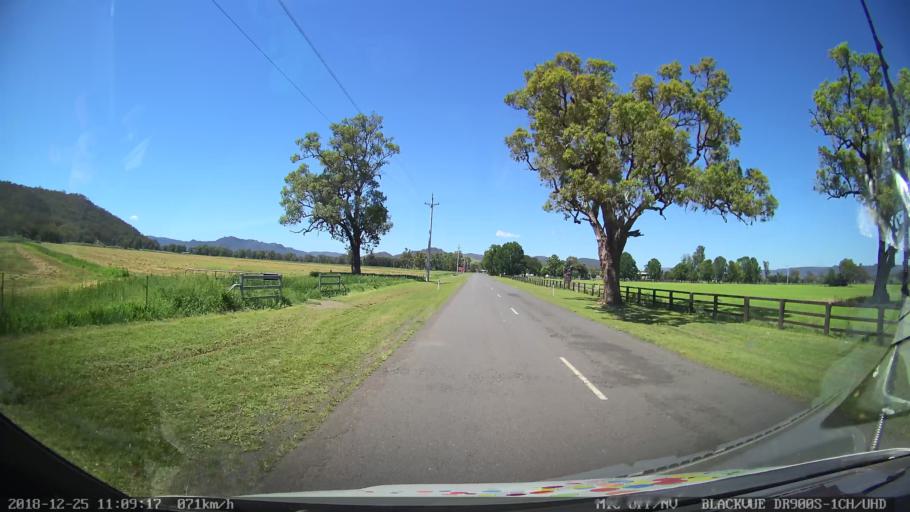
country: AU
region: New South Wales
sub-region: Upper Hunter Shire
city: Merriwa
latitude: -32.4098
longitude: 150.1191
